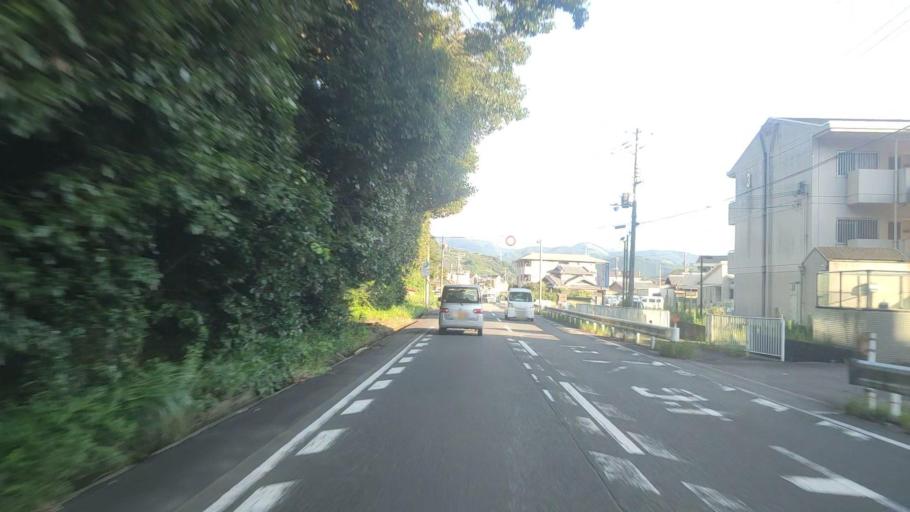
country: JP
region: Wakayama
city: Tanabe
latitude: 33.7240
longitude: 135.4448
